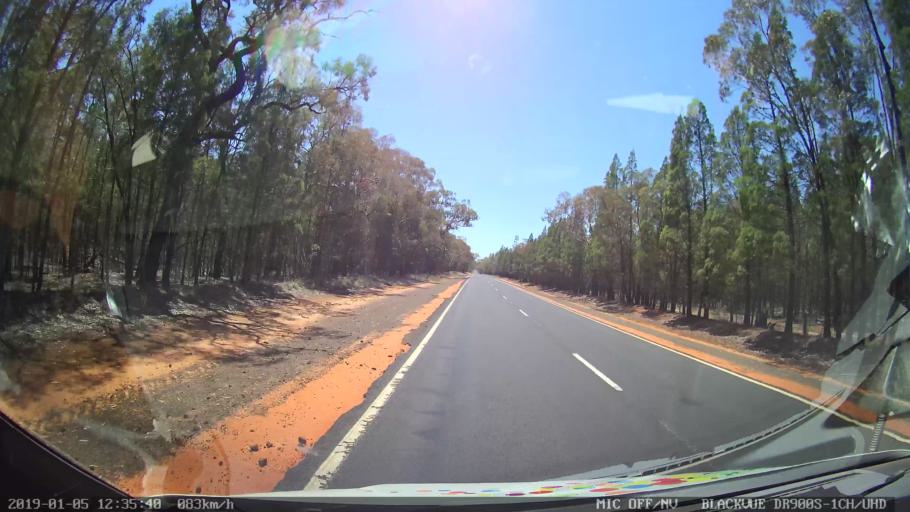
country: AU
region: New South Wales
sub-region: Warrumbungle Shire
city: Coonabarabran
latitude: -31.2090
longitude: 149.4292
